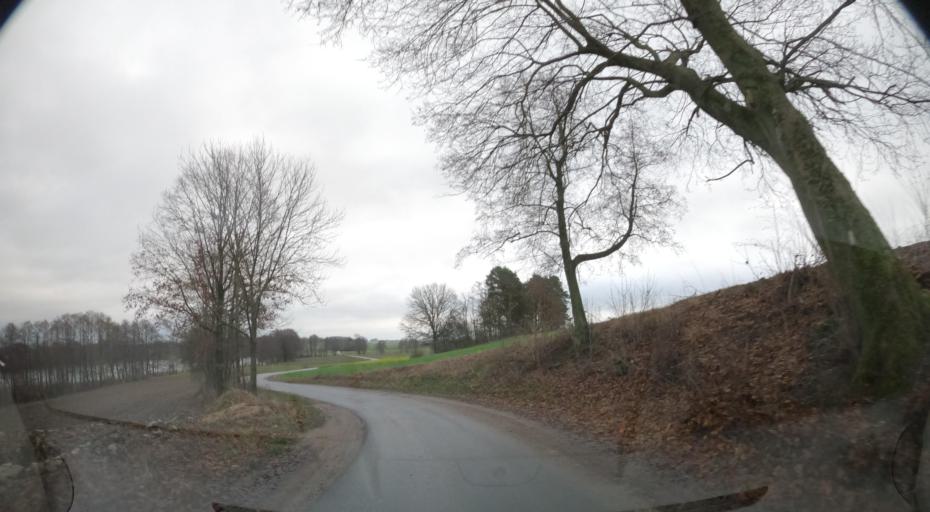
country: PL
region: Greater Poland Voivodeship
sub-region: Powiat pilski
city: Wysoka
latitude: 53.2540
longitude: 17.1409
